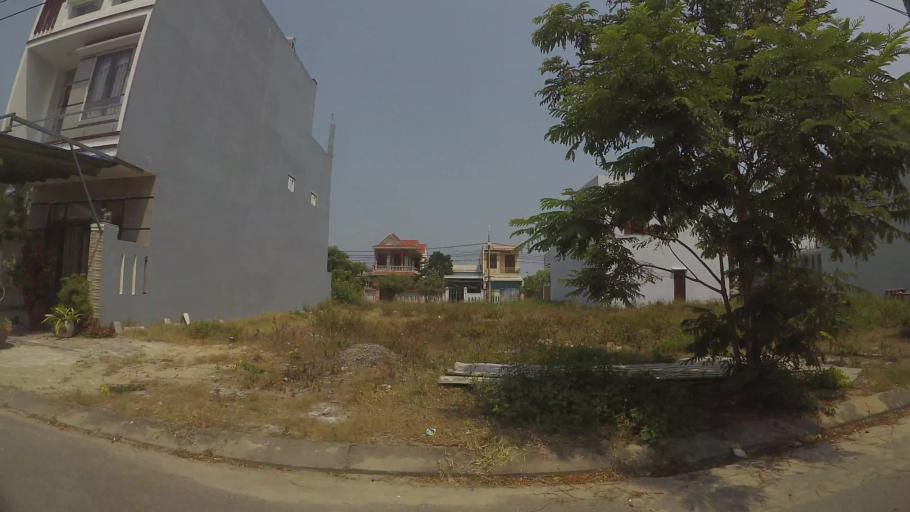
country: VN
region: Da Nang
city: Ngu Hanh Son
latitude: 15.9946
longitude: 108.2671
